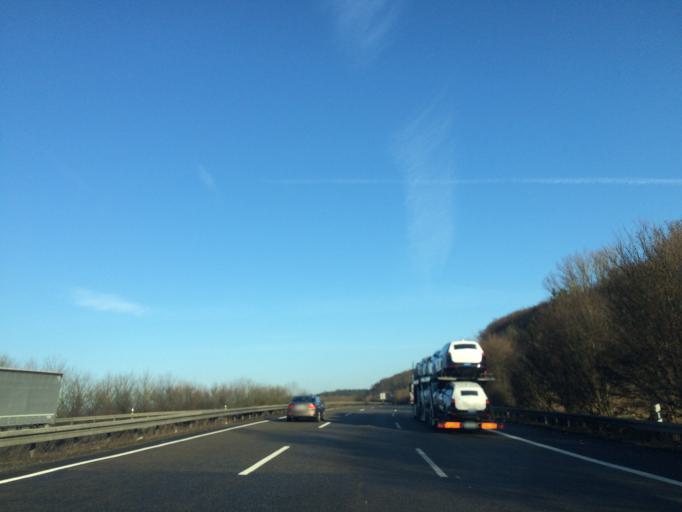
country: DE
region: Hesse
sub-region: Regierungsbezirk Kassel
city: Malsfeld
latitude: 51.0966
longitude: 9.4834
